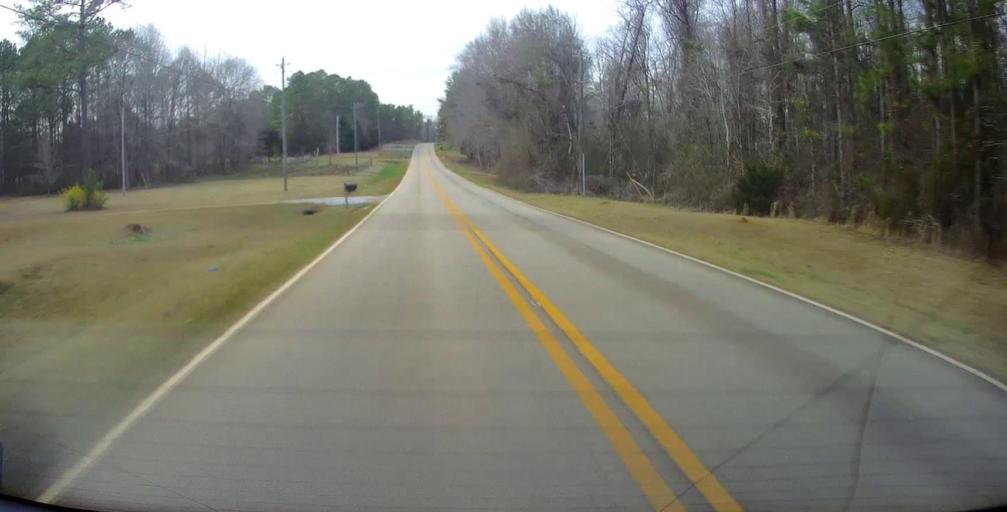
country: US
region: Georgia
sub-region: Troup County
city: West Point
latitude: 32.9407
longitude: -85.1288
